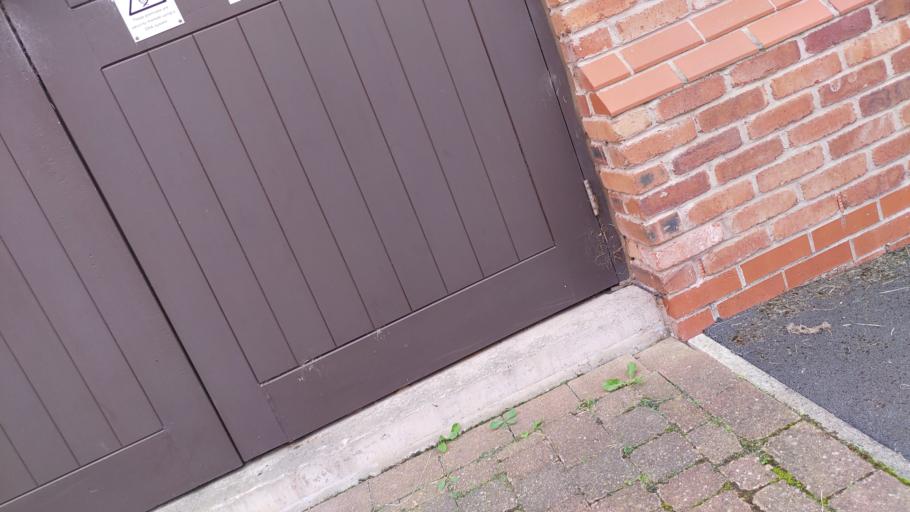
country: GB
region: England
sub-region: Lancashire
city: Coppull
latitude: 53.6302
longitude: -2.6393
